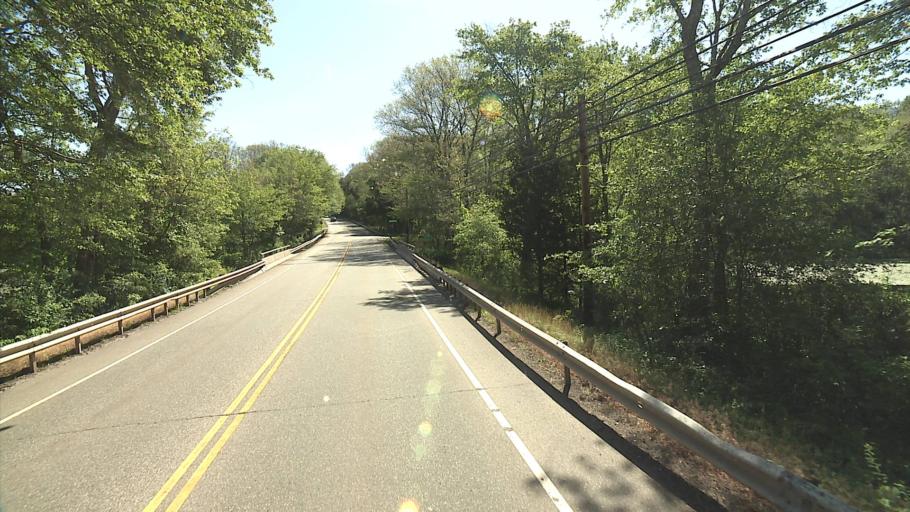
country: US
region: Connecticut
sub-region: New London County
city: Colchester
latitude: 41.5495
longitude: -72.3933
